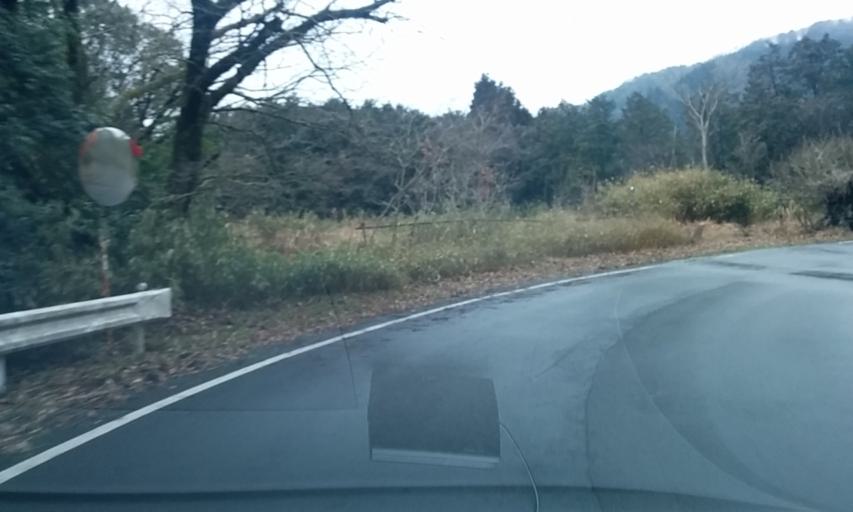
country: JP
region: Kyoto
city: Ayabe
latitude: 35.2238
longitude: 135.2380
